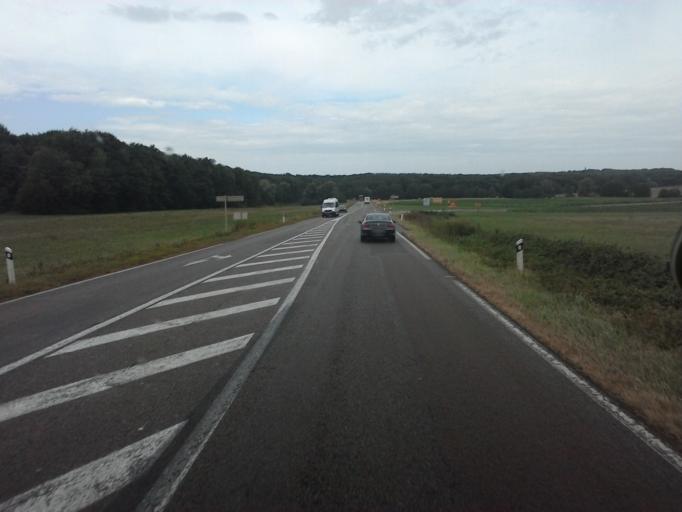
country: FR
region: Franche-Comte
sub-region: Departement du Jura
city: Poligny
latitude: 46.8454
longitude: 5.6390
